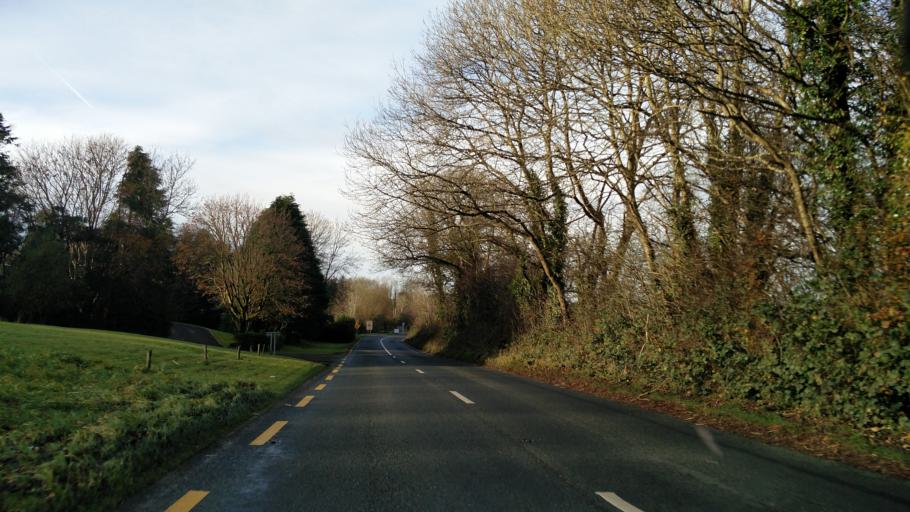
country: IE
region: Connaught
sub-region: Maigh Eo
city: Westport
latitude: 53.7886
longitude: -9.5005
